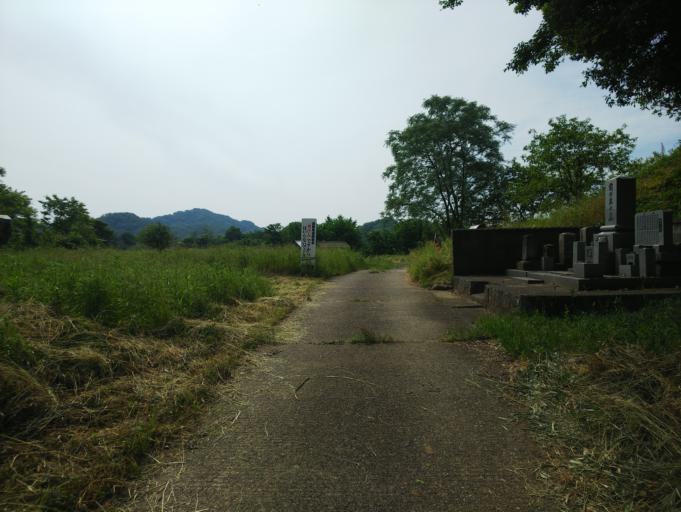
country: JP
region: Kyoto
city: Miyazu
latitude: 35.6788
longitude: 135.0307
